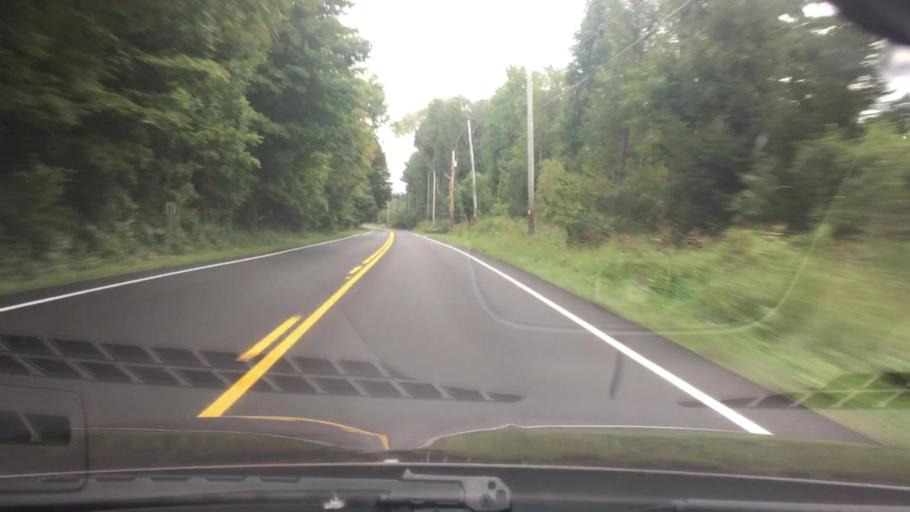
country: US
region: New York
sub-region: Dutchess County
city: Millbrook
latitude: 41.8340
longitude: -73.6147
